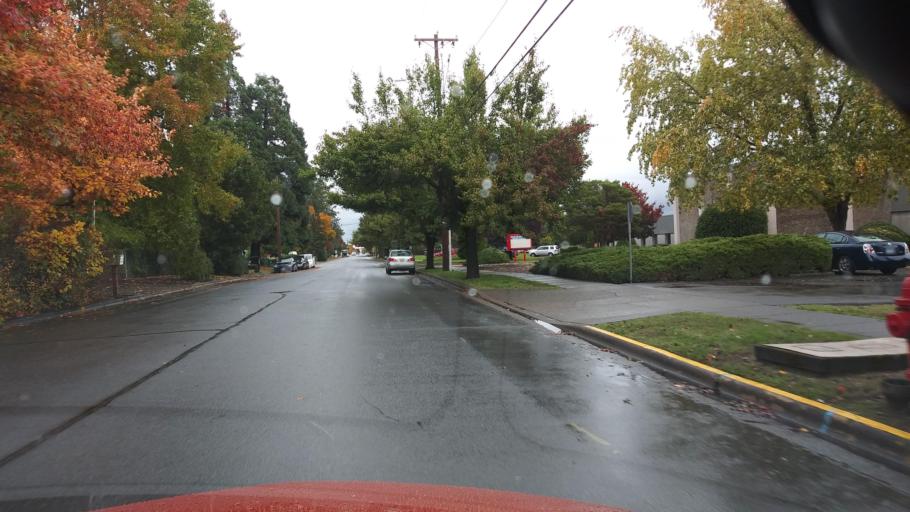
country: US
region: Oregon
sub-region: Washington County
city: Cornelius
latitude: 45.5149
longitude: -123.0758
